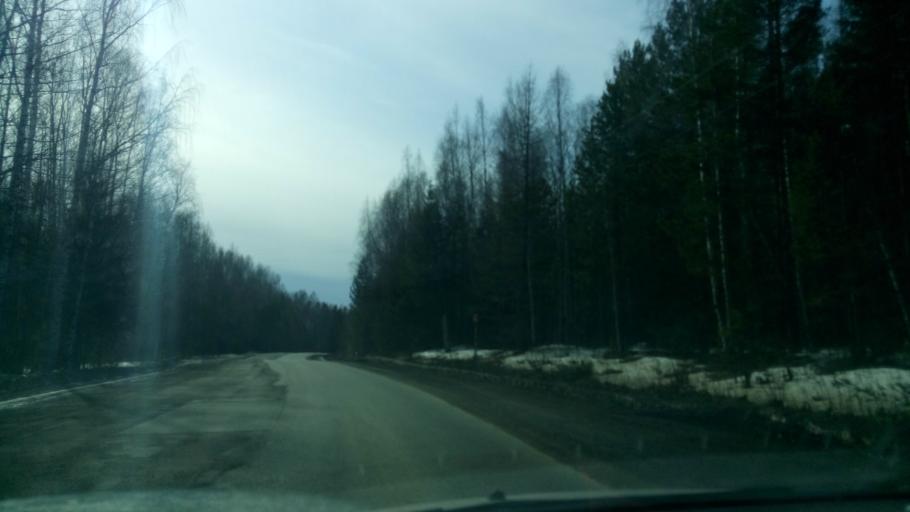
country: RU
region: Sverdlovsk
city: Chernoistochinsk
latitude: 57.7074
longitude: 59.7762
